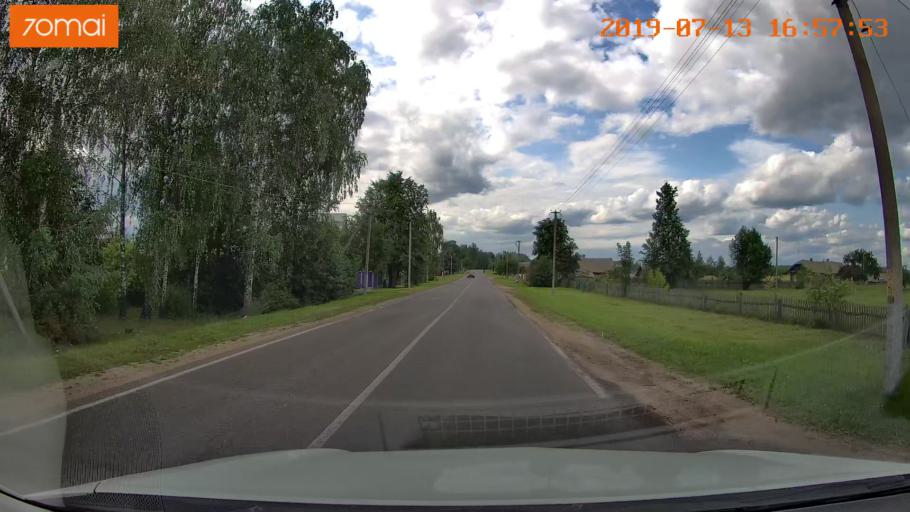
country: BY
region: Mogilev
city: Kirawsk
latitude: 53.2836
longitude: 29.4473
